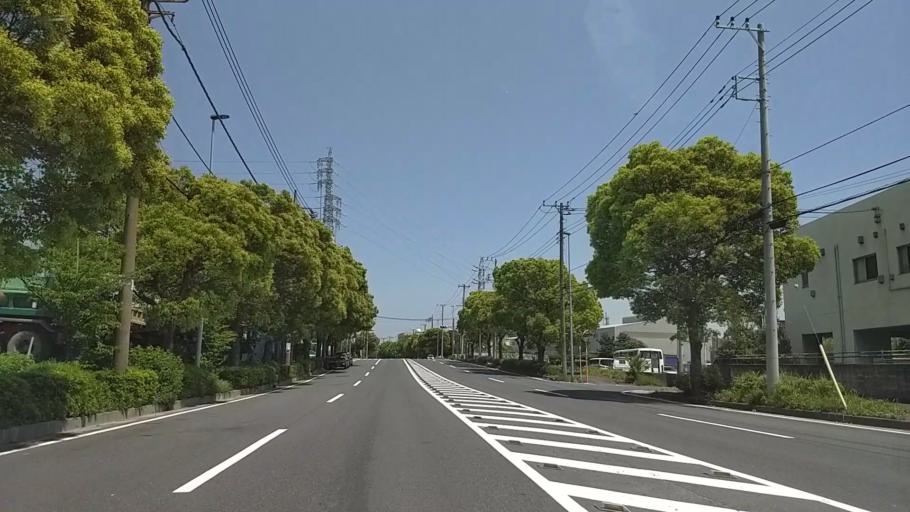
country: JP
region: Kanagawa
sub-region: Kawasaki-shi
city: Kawasaki
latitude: 35.5201
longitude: 139.7424
